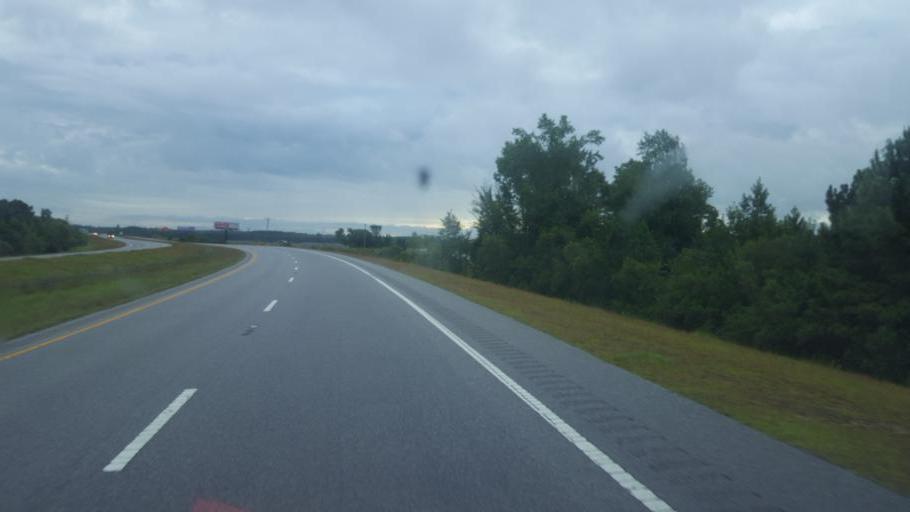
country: US
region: North Carolina
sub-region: Tyrrell County
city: Columbia
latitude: 35.9032
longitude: -76.3018
